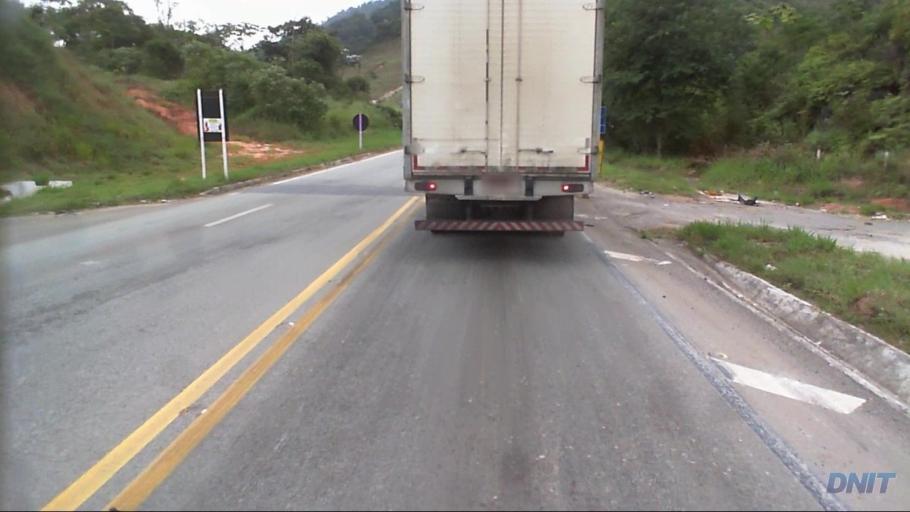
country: BR
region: Minas Gerais
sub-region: Nova Era
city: Nova Era
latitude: -19.6560
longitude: -42.9581
